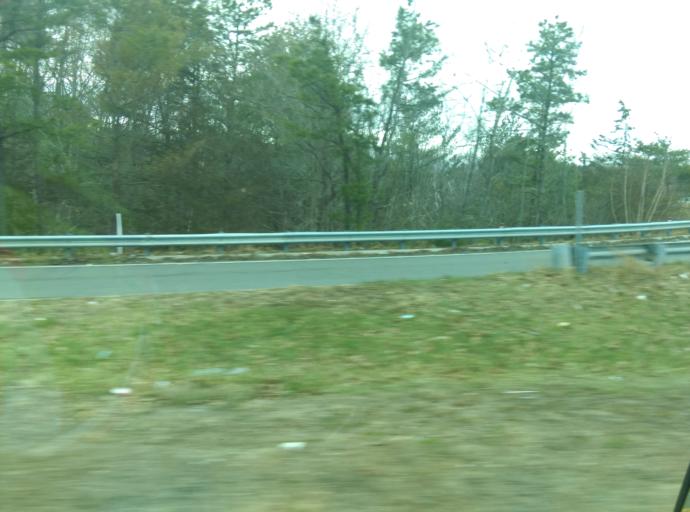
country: US
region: Massachusetts
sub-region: Essex County
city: Amesbury
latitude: 42.8389
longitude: -70.9344
